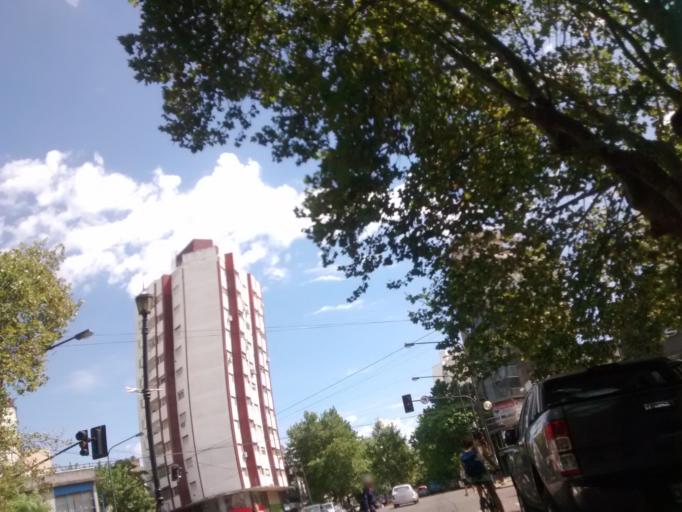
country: AR
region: Buenos Aires
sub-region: Partido de La Plata
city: La Plata
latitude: -34.9147
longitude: -57.9549
